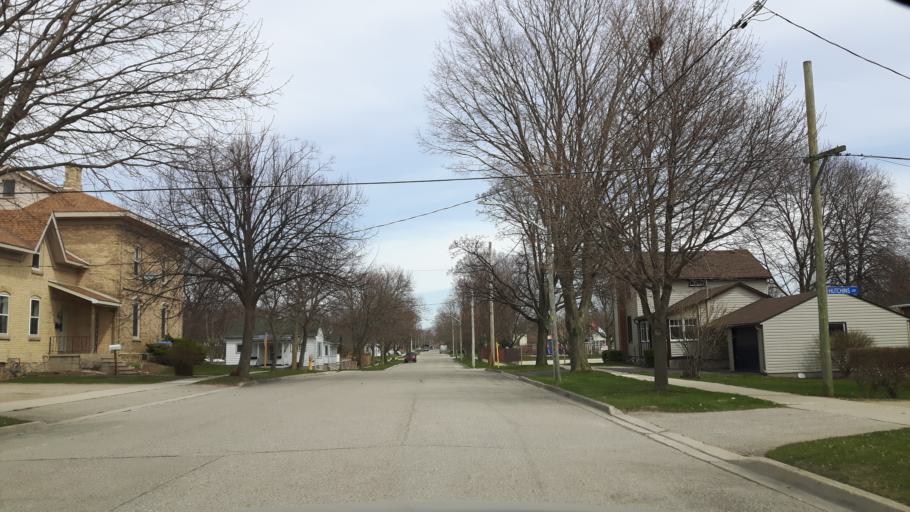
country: CA
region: Ontario
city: Goderich
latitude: 43.7371
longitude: -81.7133
